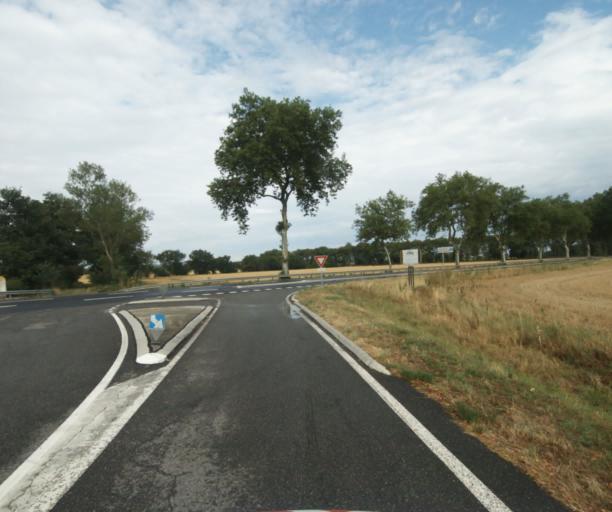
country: FR
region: Midi-Pyrenees
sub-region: Departement de la Haute-Garonne
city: Revel
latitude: 43.4264
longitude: 1.9546
